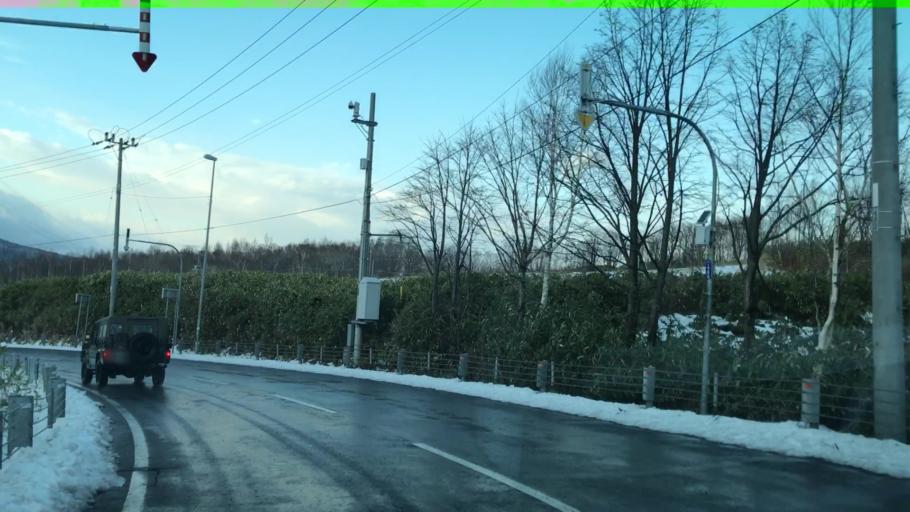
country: JP
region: Hokkaido
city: Otaru
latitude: 43.0918
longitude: 140.9754
